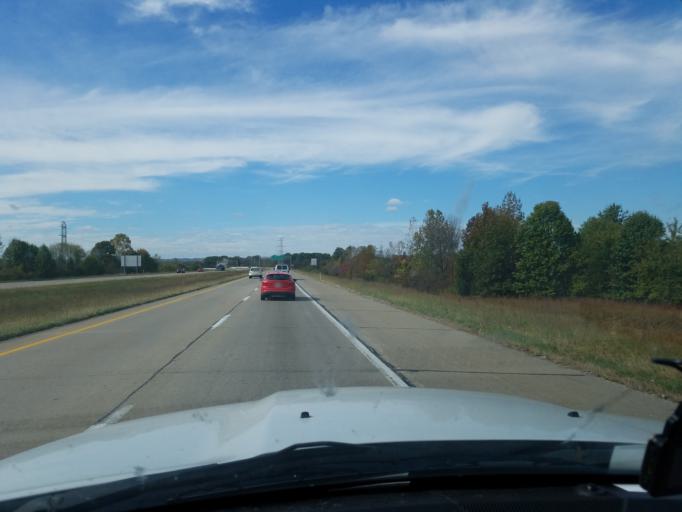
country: US
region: Indiana
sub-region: Clark County
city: Oak Park
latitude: 38.3472
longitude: -85.7248
